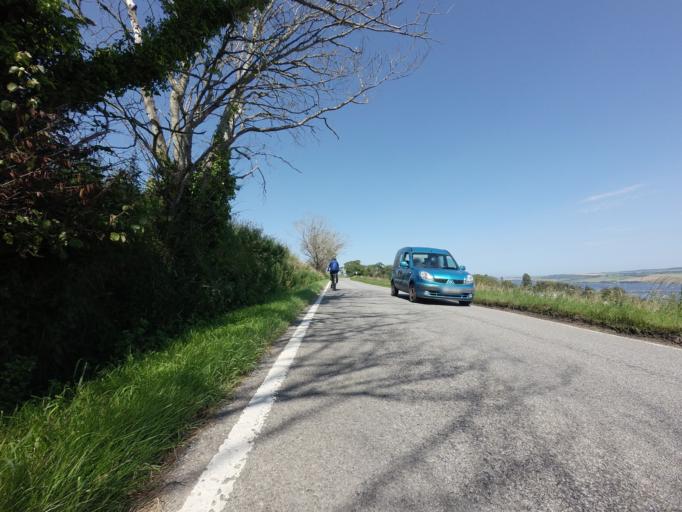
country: GB
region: Scotland
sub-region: Highland
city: Dingwall
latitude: 57.6188
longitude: -4.4032
